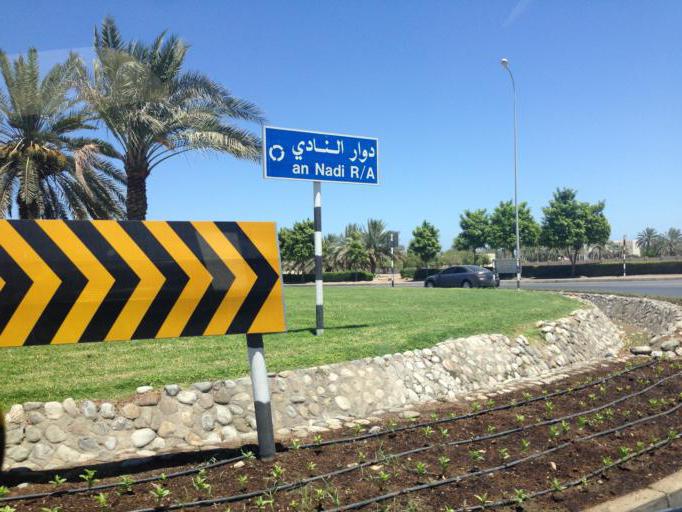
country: OM
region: Muhafazat Masqat
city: As Sib al Jadidah
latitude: 23.6486
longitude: 58.2022
